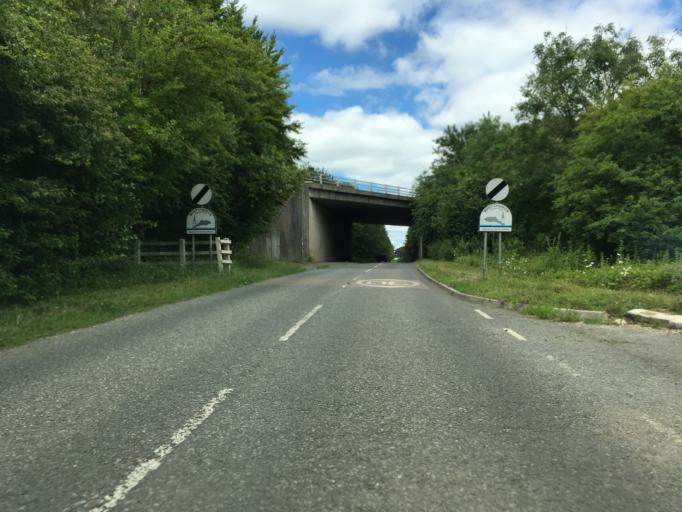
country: GB
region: England
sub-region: Hampshire
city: Overton
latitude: 51.2343
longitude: -1.3479
